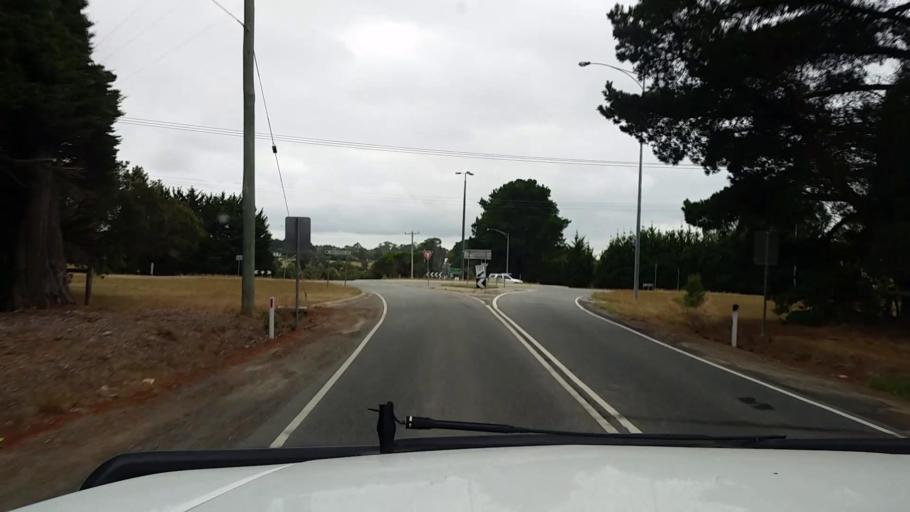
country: AU
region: Victoria
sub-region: Mornington Peninsula
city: Hastings
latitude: -38.2854
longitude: 145.1456
